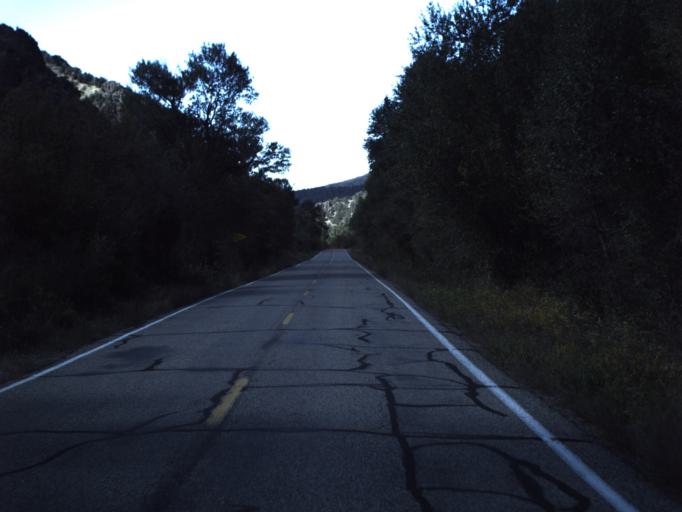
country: US
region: Utah
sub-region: Beaver County
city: Beaver
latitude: 38.2743
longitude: -112.5538
